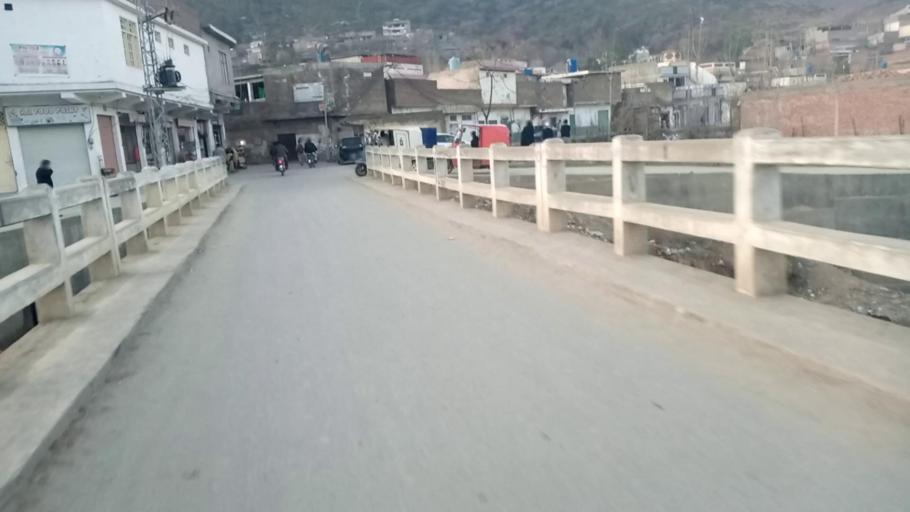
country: PK
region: Khyber Pakhtunkhwa
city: Saidu Sharif
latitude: 34.7476
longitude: 72.3499
